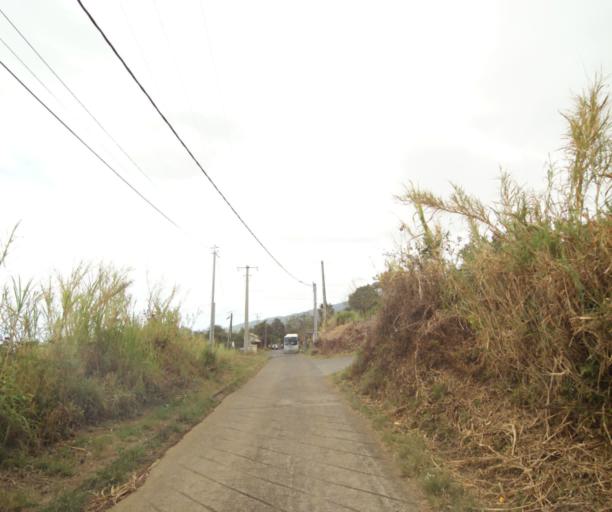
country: RE
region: Reunion
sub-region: Reunion
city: Saint-Paul
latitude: -21.0140
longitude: 55.3356
